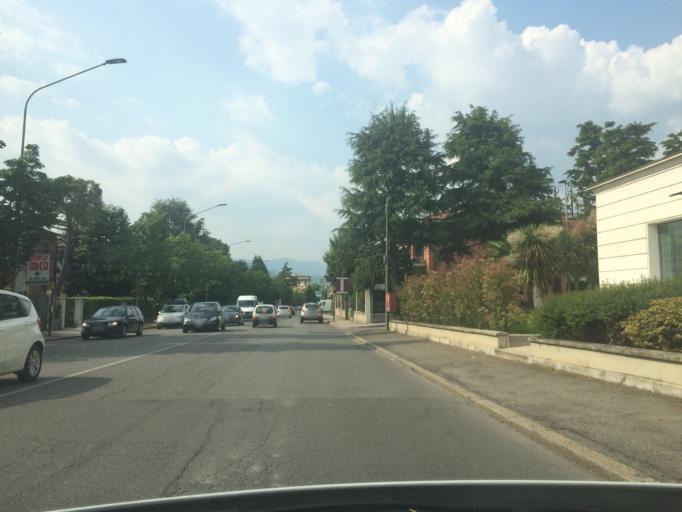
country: IT
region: Lombardy
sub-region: Provincia di Brescia
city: Brescia
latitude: 45.5446
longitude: 10.2303
